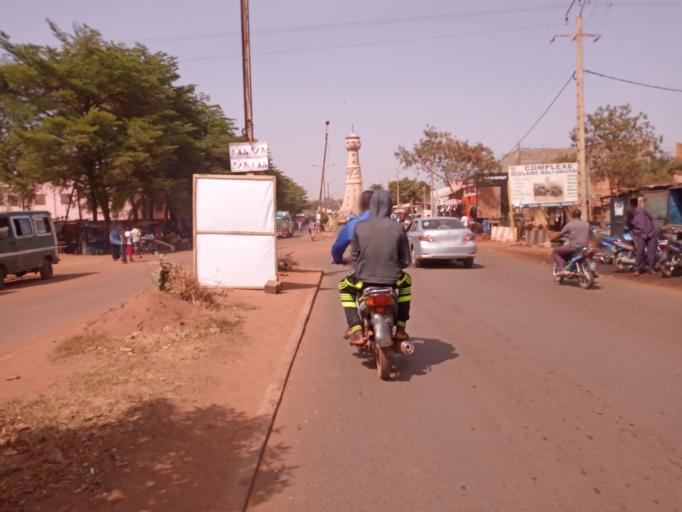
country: ML
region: Bamako
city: Bamako
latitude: 12.5826
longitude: -7.9449
